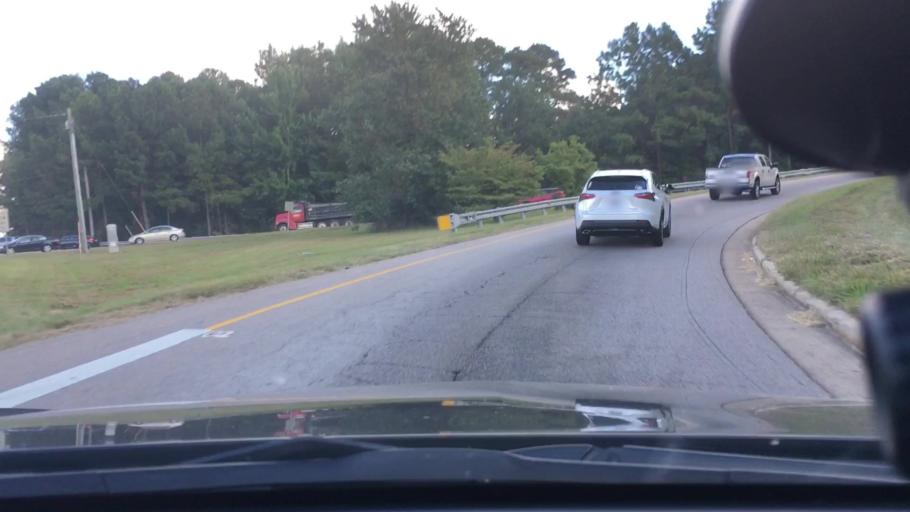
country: US
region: North Carolina
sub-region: Wake County
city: West Raleigh
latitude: 35.8032
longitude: -78.6926
